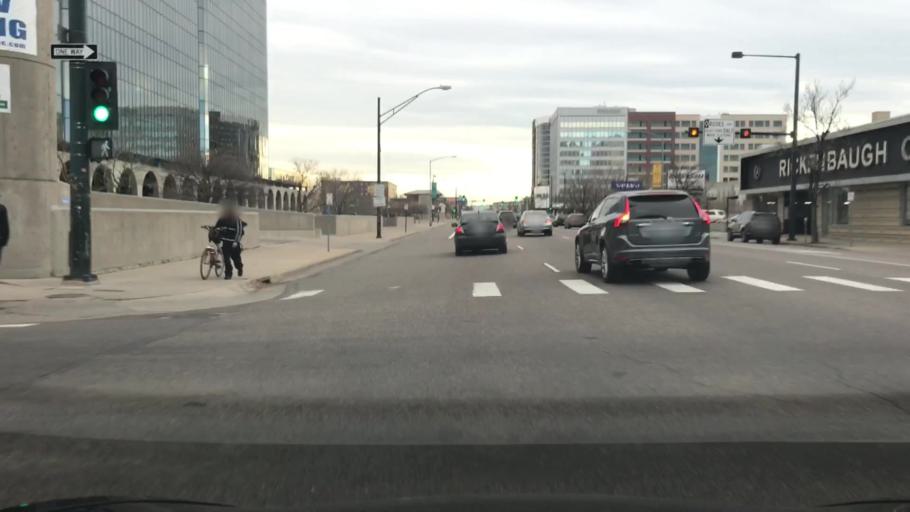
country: US
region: Colorado
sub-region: Denver County
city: Denver
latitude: 39.7291
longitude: -104.9873
